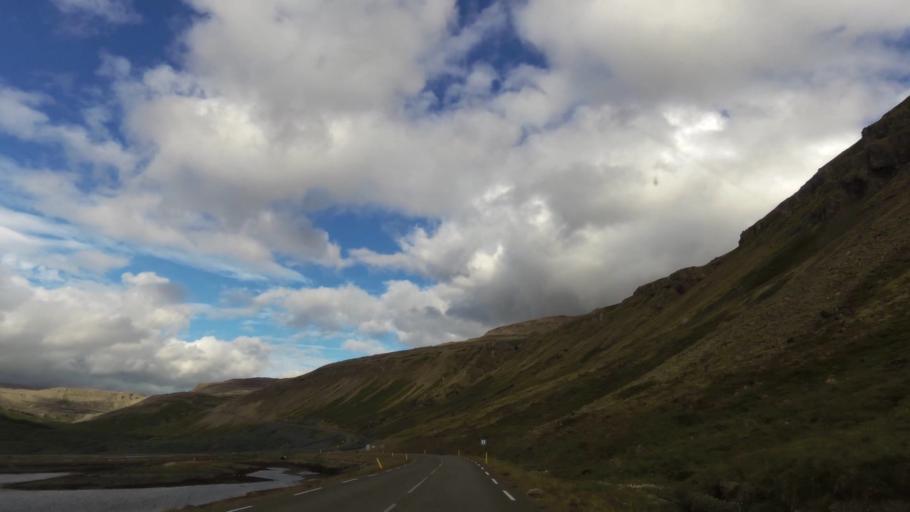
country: IS
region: West
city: Olafsvik
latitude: 65.5304
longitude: -23.7884
